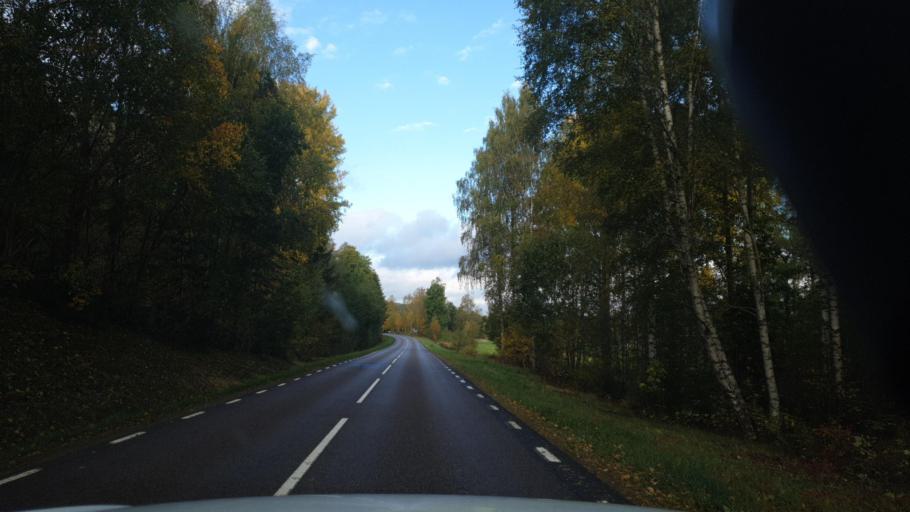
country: SE
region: Vaermland
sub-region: Arvika Kommun
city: Arvika
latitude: 59.4837
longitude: 12.6987
